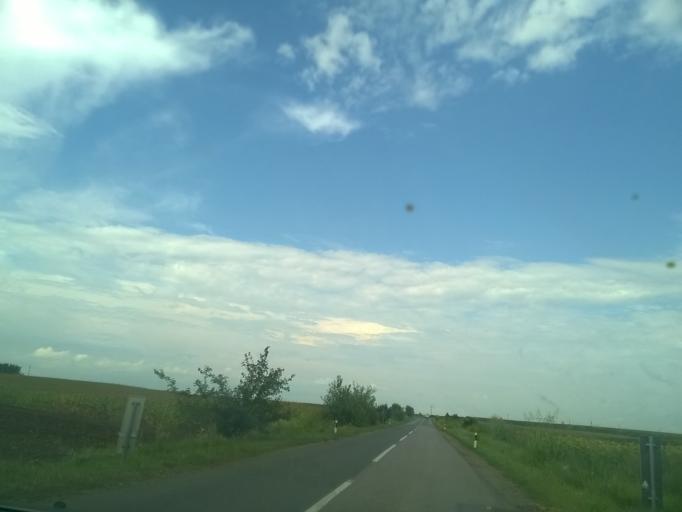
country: RS
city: Orlovat
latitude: 45.2504
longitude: 20.5736
